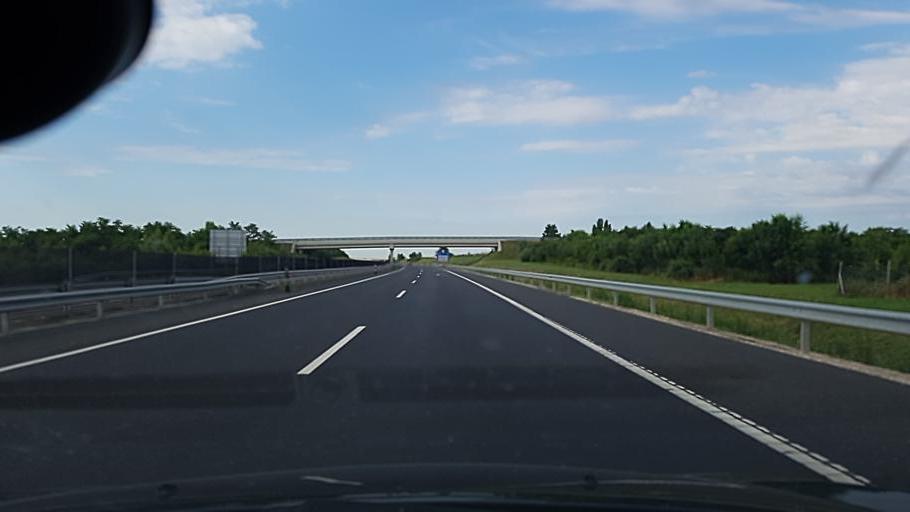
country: HU
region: Pest
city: Szazhalombatta
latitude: 47.3156
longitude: 18.8702
